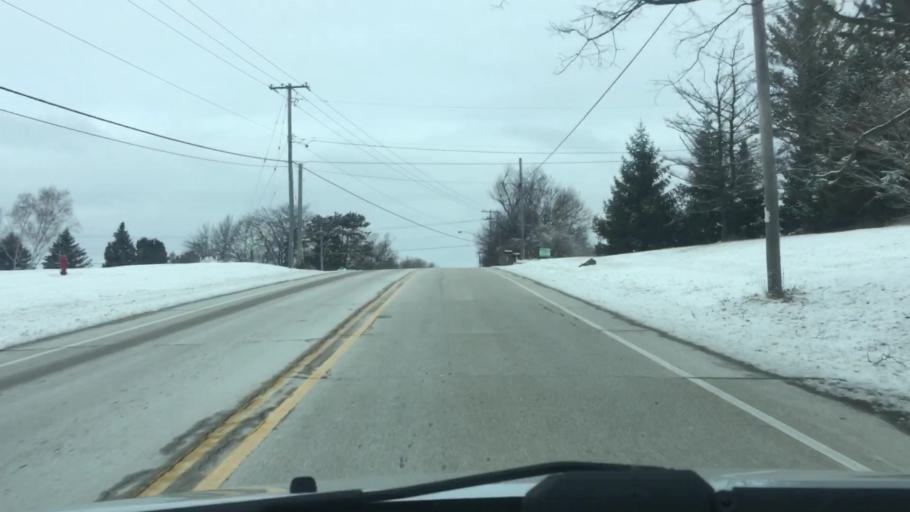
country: US
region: Wisconsin
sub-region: Waukesha County
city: Brookfield
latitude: 43.0776
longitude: -88.1059
